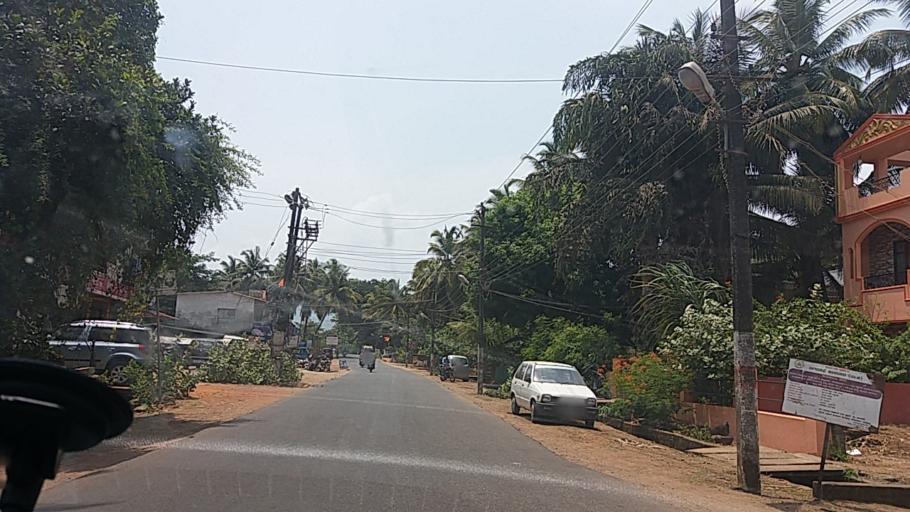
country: IN
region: Karnataka
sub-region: Uttar Kannada
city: Karwar
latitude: 14.8114
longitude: 74.1450
